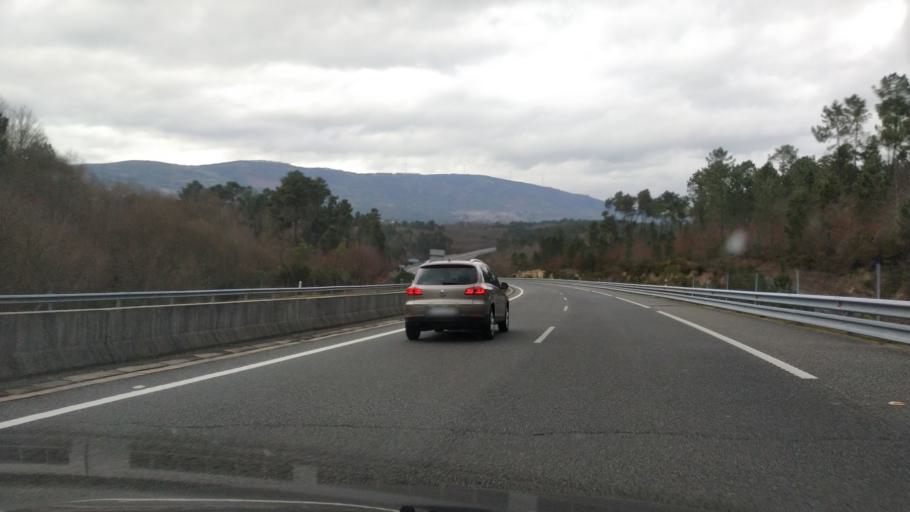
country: ES
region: Galicia
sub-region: Provincia de Ourense
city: Cea
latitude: 42.4586
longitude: -8.0234
